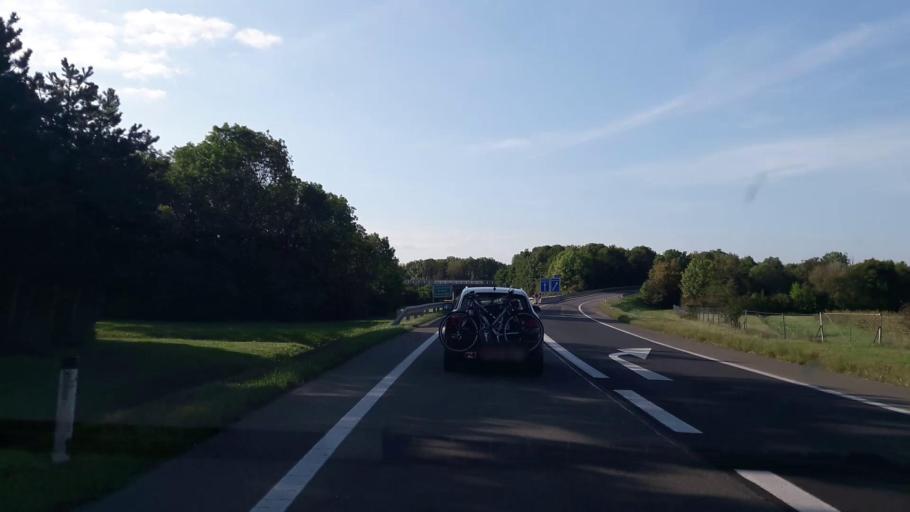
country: AT
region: Burgenland
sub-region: Eisenstadt-Umgebung
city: Wulkaprodersdorf
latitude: 47.8167
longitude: 16.4926
